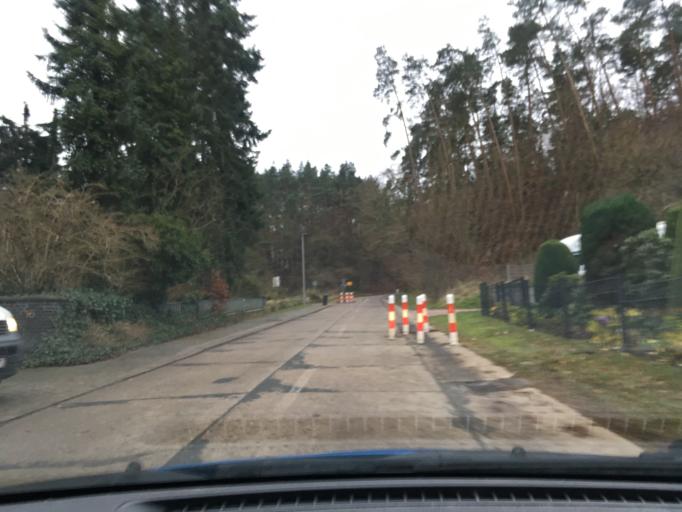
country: DE
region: Lower Saxony
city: Tosterglope
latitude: 53.2623
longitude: 10.8058
